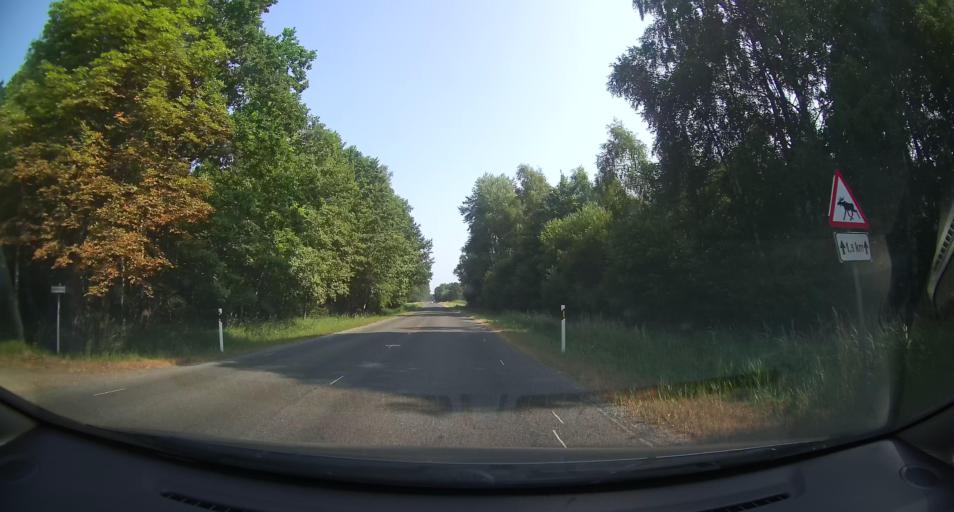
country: EE
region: Paernumaa
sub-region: Audru vald
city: Audru
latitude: 58.4460
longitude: 24.3096
